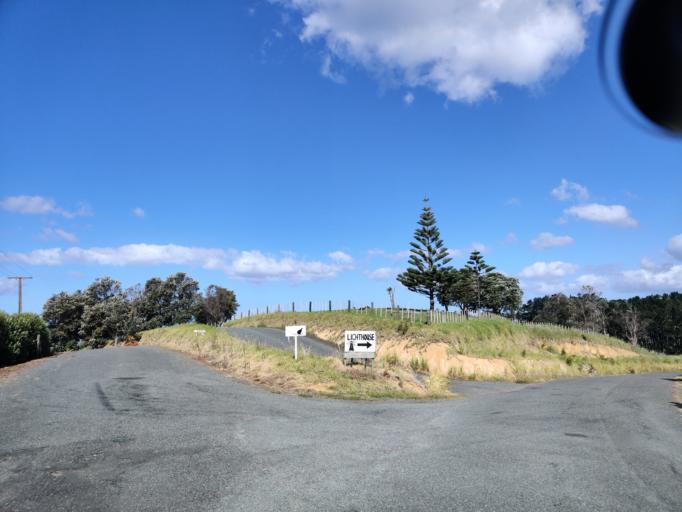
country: NZ
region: Northland
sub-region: Whangarei
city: Ngunguru
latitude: -35.6077
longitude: 174.5283
